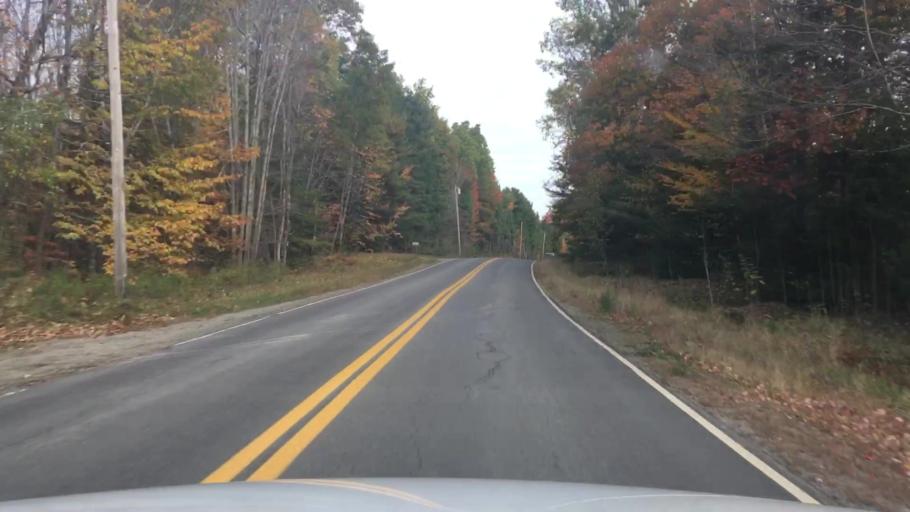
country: US
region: Maine
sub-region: Waldo County
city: Searsmont
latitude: 44.4056
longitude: -69.1377
